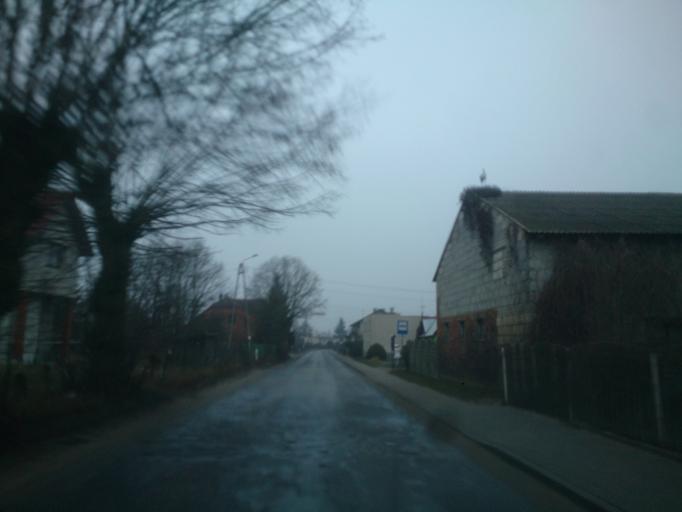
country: PL
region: Pomeranian Voivodeship
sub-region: Powiat starogardzki
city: Lubichowo
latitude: 53.8321
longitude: 18.4330
